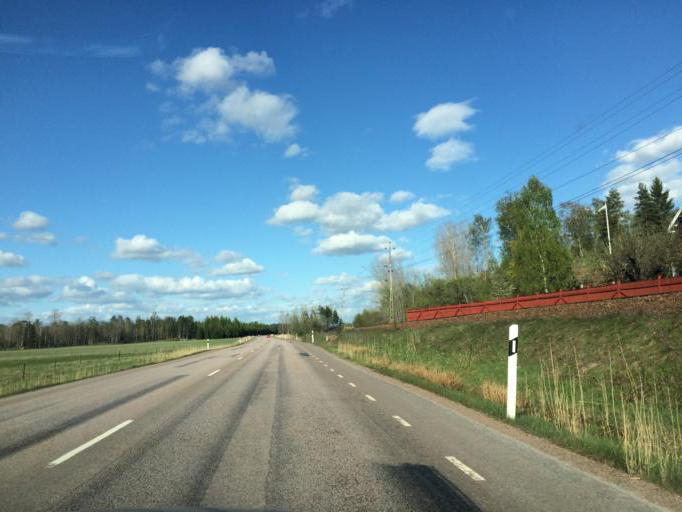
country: SE
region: Vaestmanland
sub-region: Hallstahammars Kommun
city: Kolback
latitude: 59.5490
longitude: 16.1866
